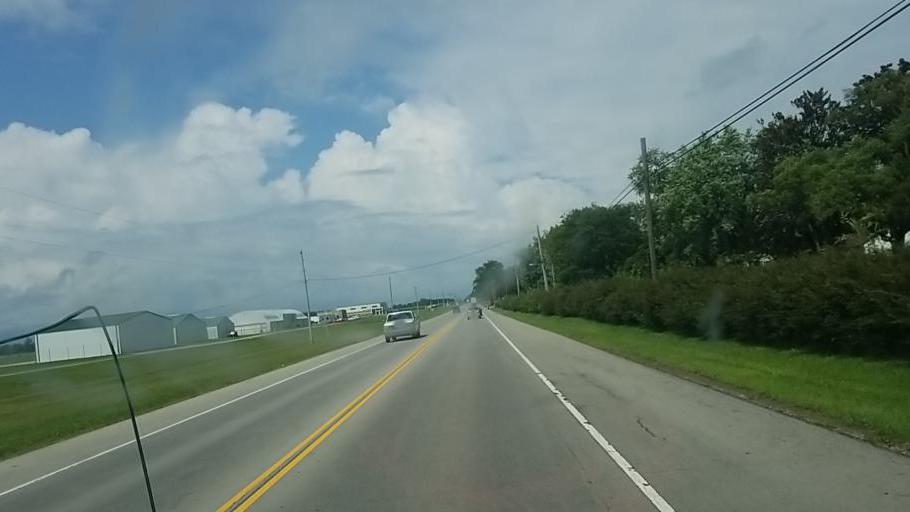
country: US
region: Ohio
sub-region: Champaign County
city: Urbana
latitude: 40.1293
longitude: -83.7484
